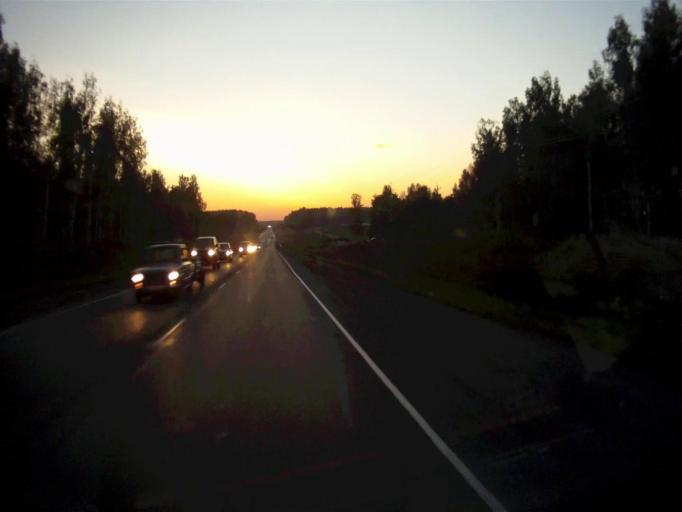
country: RU
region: Chelyabinsk
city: Poletayevo
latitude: 55.2186
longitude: 61.0354
